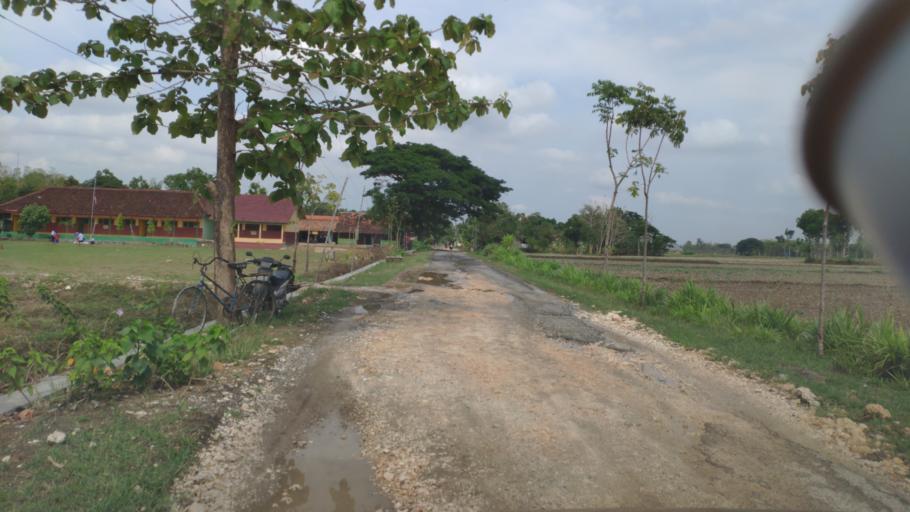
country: ID
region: Central Java
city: Klopoduwur
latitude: -7.0206
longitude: 111.4052
